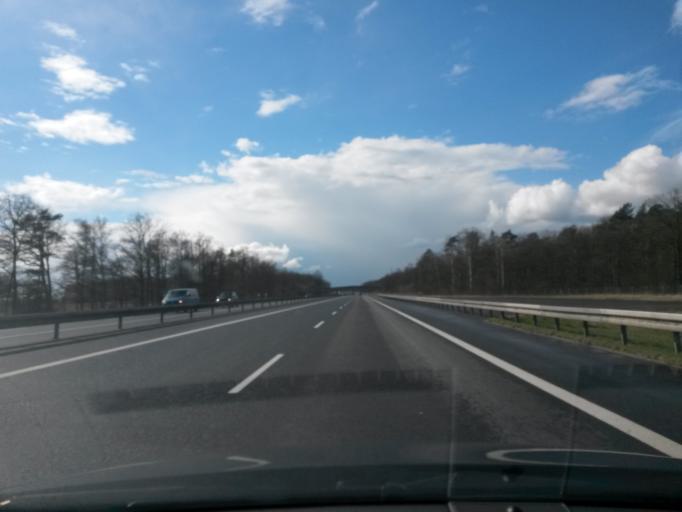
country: PL
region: Greater Poland Voivodeship
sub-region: Powiat wrzesinski
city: Wrzesnia
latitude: 52.3045
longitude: 17.6093
